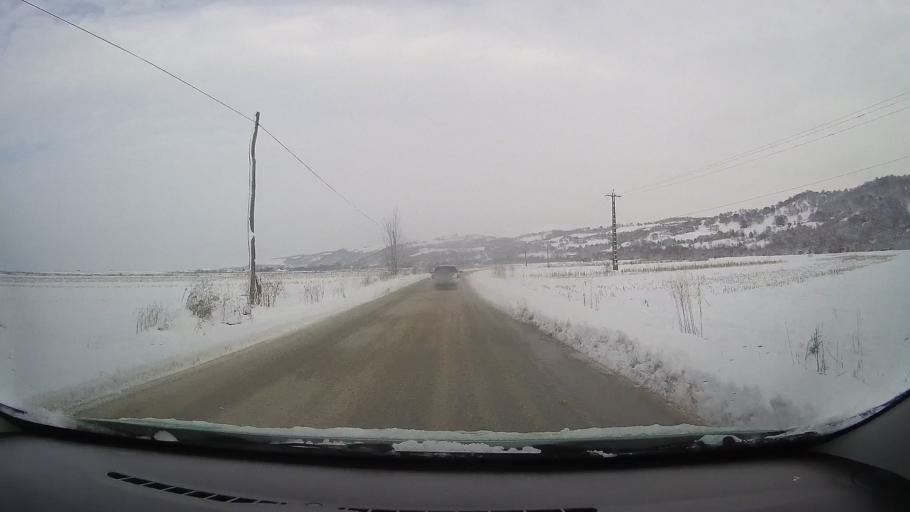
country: RO
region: Alba
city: Pianu de Sus
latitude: 45.9151
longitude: 23.4833
